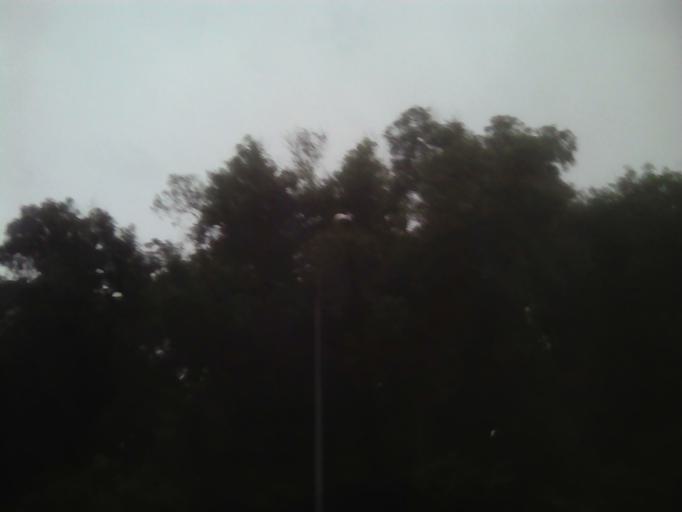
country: MY
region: Penang
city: Perai
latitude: 5.3970
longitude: 100.4157
